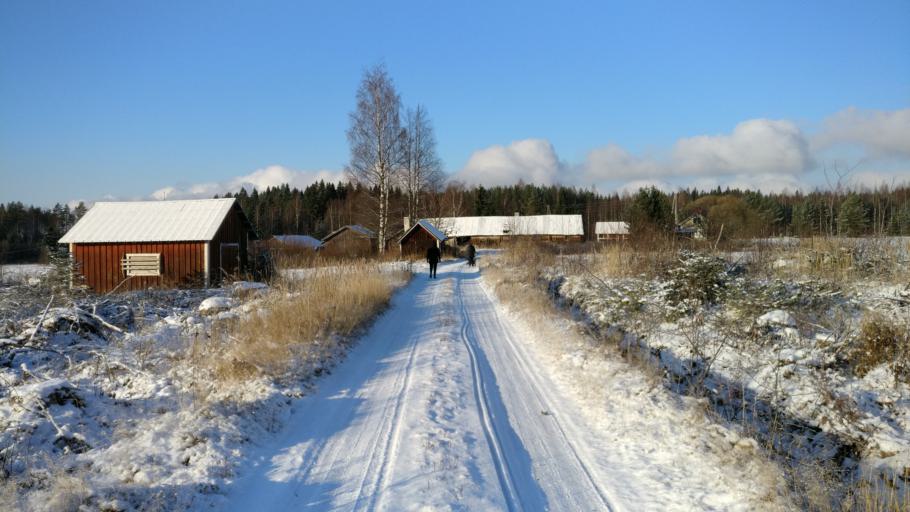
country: FI
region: Central Finland
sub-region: Jyvaeskylae
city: Hankasalmi
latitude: 62.4250
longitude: 26.6724
